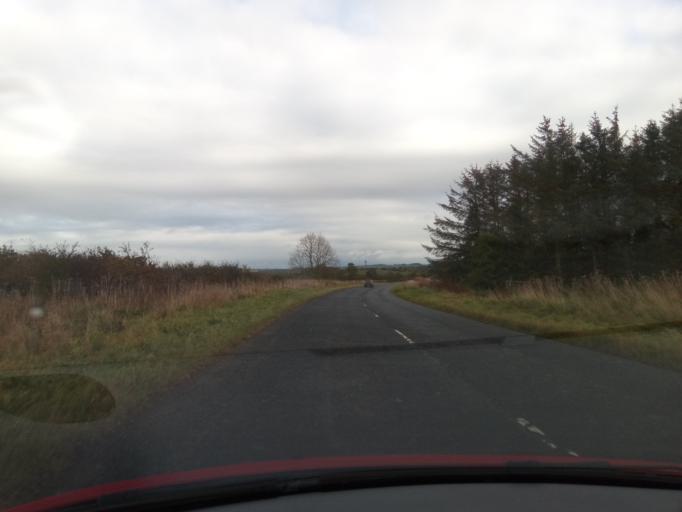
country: GB
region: Scotland
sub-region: The Scottish Borders
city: Newtown St Boswells
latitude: 55.5663
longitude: -2.6701
